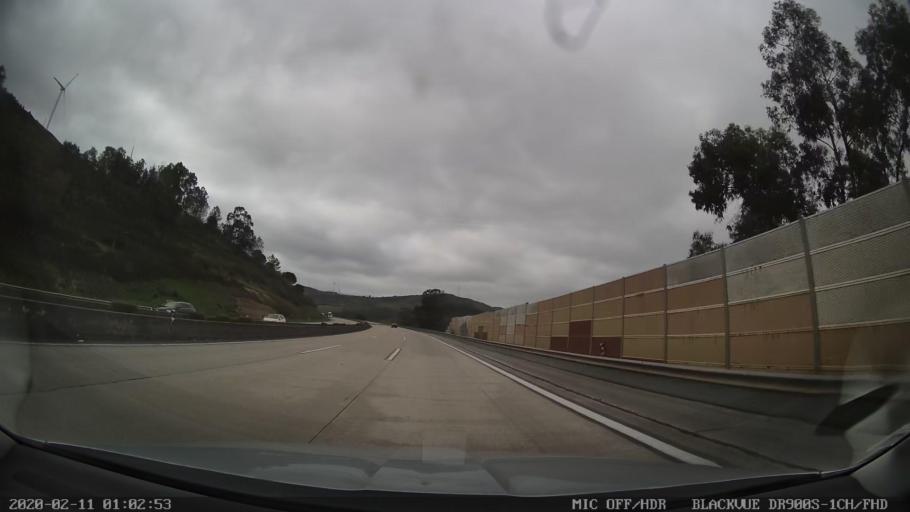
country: PT
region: Lisbon
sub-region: Loures
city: Bucelas
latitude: 38.9008
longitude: -9.1079
